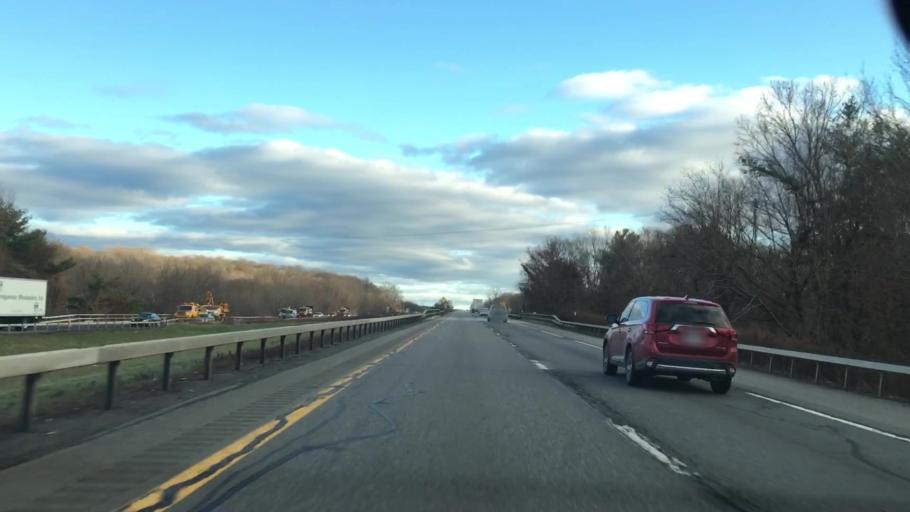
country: US
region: New York
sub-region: Putnam County
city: Brewster
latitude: 41.4113
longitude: -73.6148
